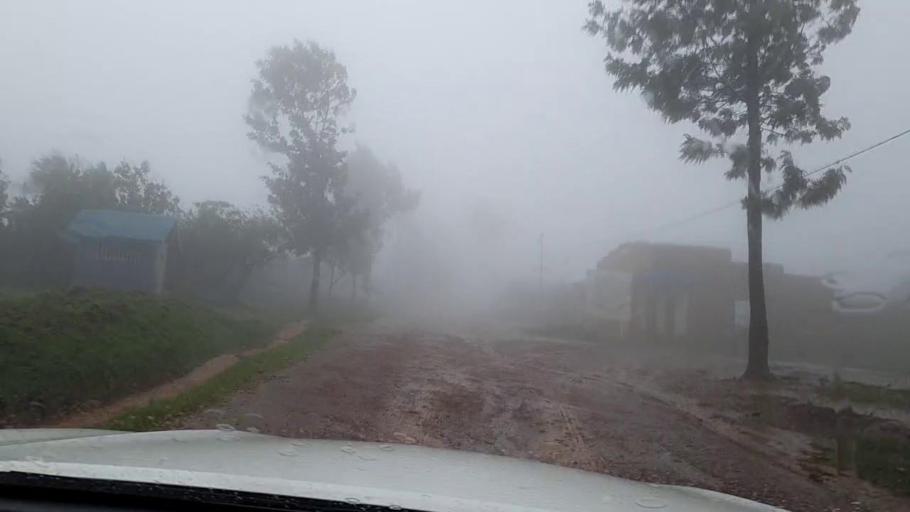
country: RW
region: Northern Province
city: Byumba
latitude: -1.7346
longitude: 30.0287
